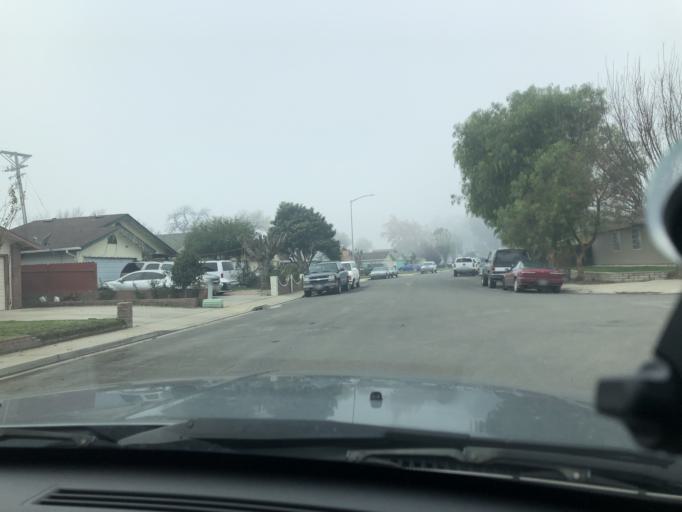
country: US
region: California
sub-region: Monterey County
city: King City
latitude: 36.2043
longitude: -121.1421
